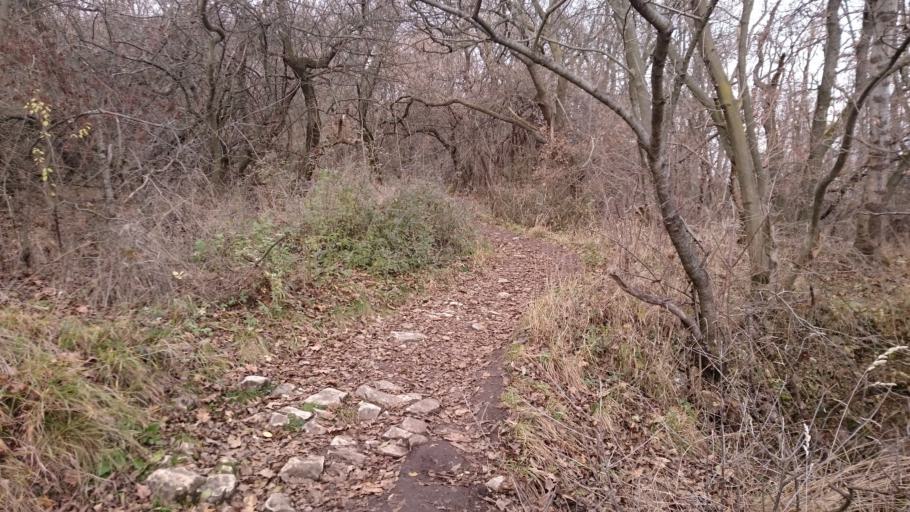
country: HU
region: Pest
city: Pilisborosjeno
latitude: 47.6199
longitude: 18.9891
